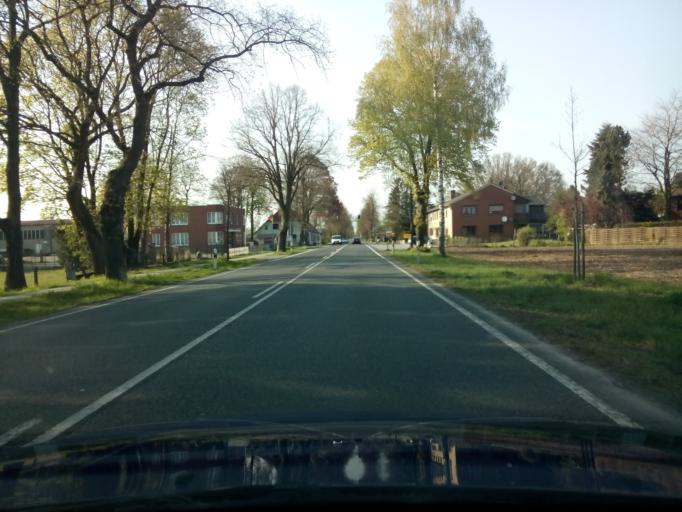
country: DE
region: Lower Saxony
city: Syke
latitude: 52.9698
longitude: 8.7950
